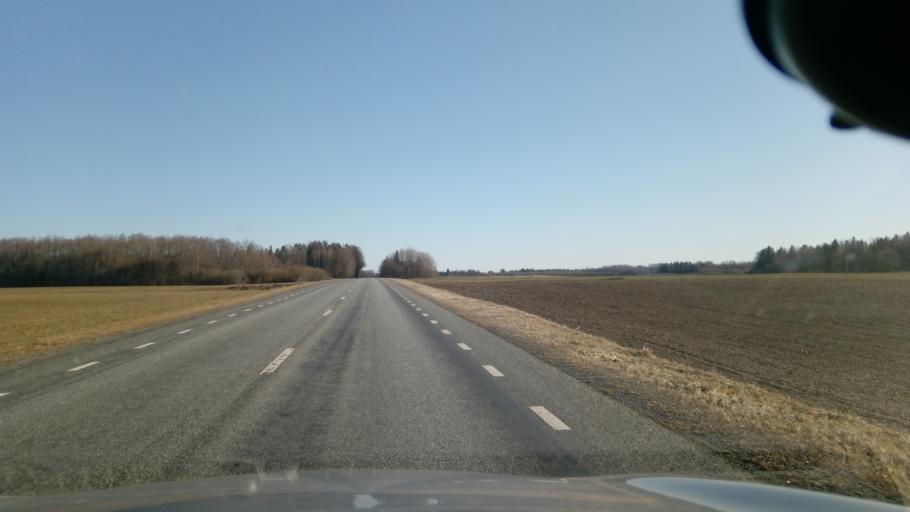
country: EE
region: Jaervamaa
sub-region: Jaerva-Jaani vald
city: Jarva-Jaani
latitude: 59.0875
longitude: 25.9735
